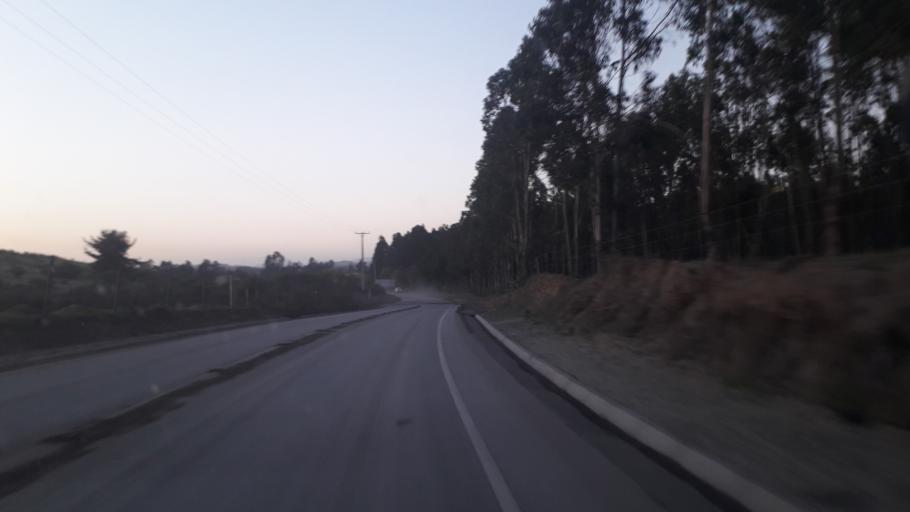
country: CL
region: Valparaiso
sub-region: Provincia de Quillota
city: Hacienda La Calera
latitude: -32.7442
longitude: -71.4180
